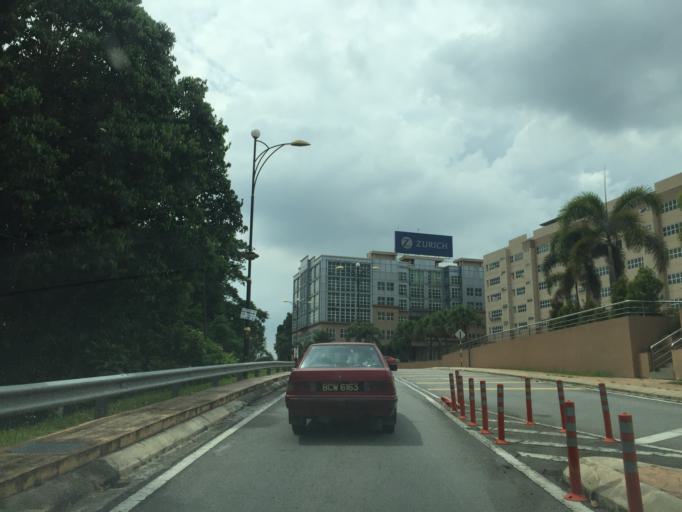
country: MY
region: Selangor
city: Klang
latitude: 3.0424
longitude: 101.4439
